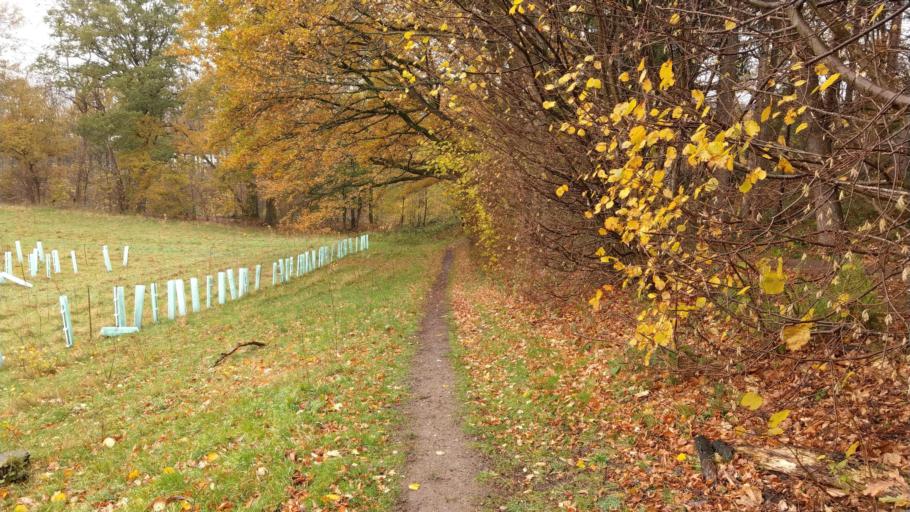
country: BE
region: Wallonia
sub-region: Province de Liege
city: La Calamine
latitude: 50.7375
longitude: 6.0514
